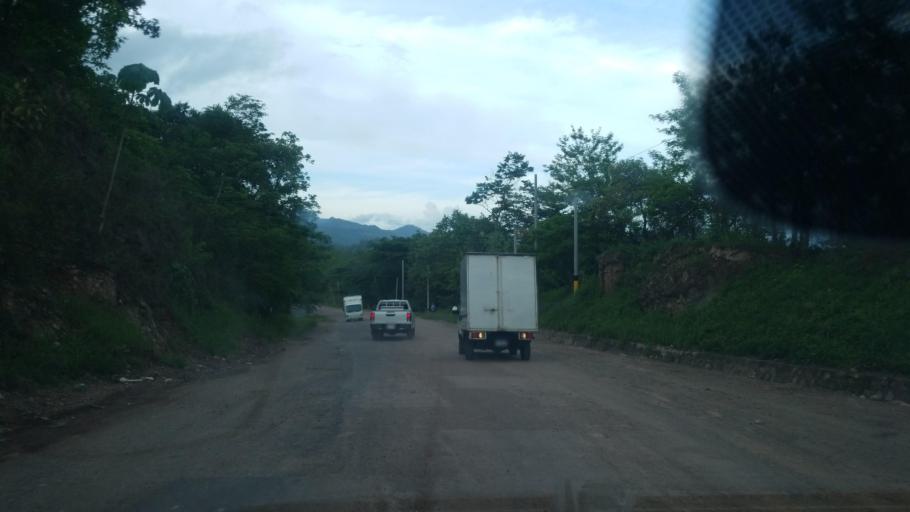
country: HN
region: Santa Barbara
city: Concepcion del Sur
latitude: 14.7988
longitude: -88.1502
